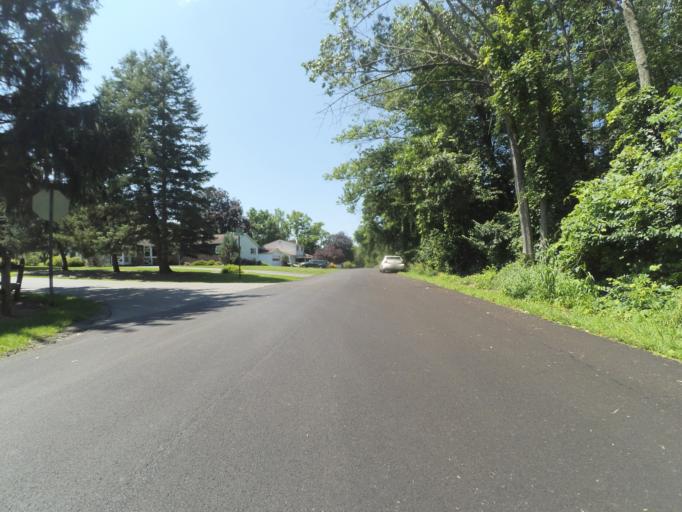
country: US
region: Pennsylvania
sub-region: Centre County
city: Pleasant Gap
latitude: 40.8651
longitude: -77.7396
